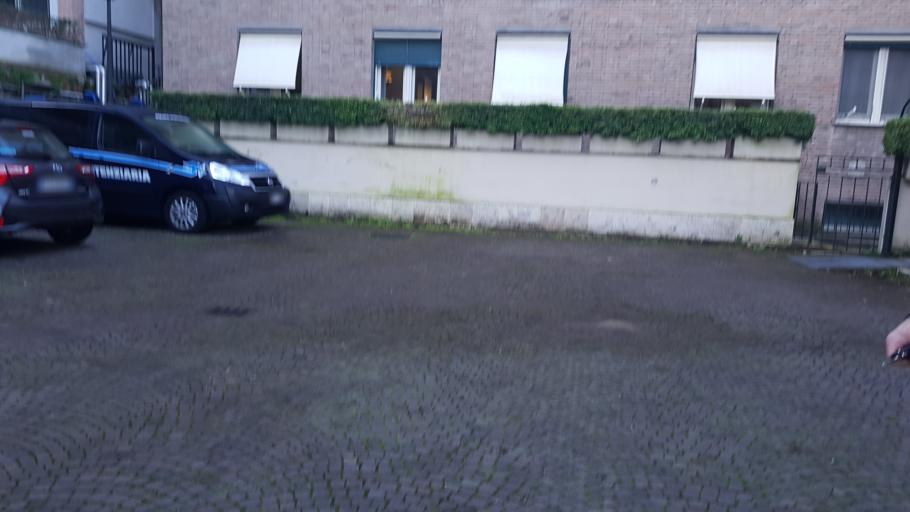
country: VA
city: Vatican City
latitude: 41.9500
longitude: 12.4540
